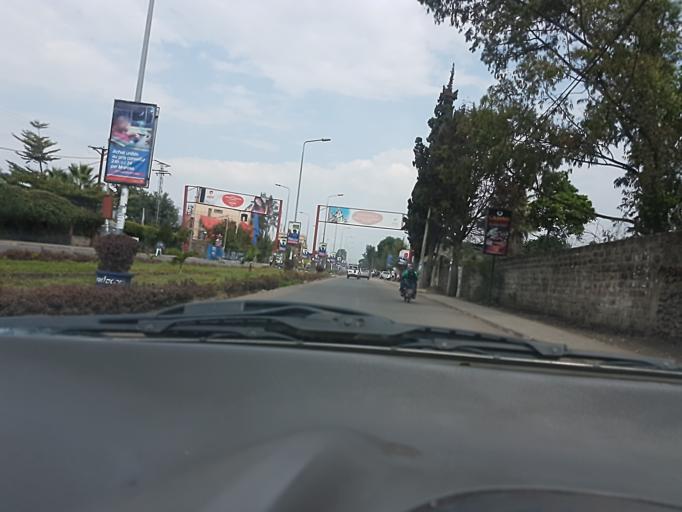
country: RW
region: Western Province
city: Gisenyi
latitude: -1.6960
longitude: 29.2400
